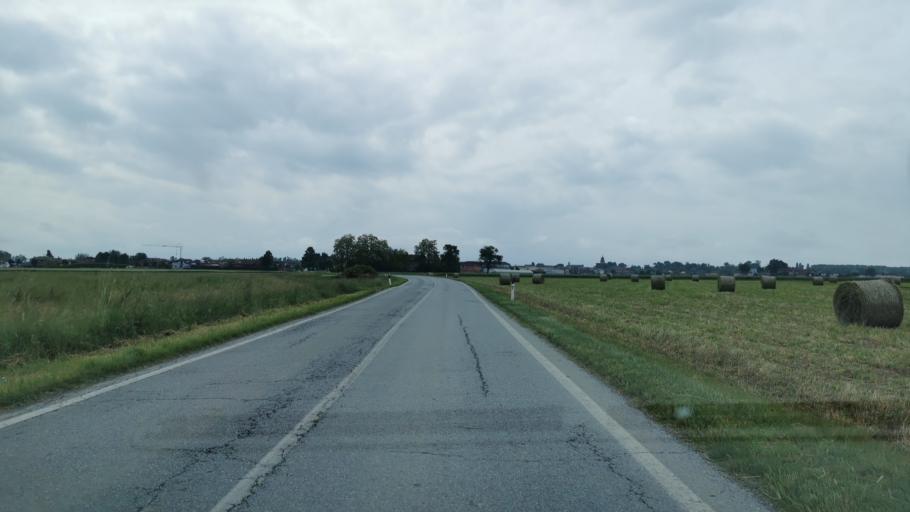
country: IT
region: Piedmont
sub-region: Provincia di Cuneo
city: Villafalletto
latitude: 44.5574
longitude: 7.5345
